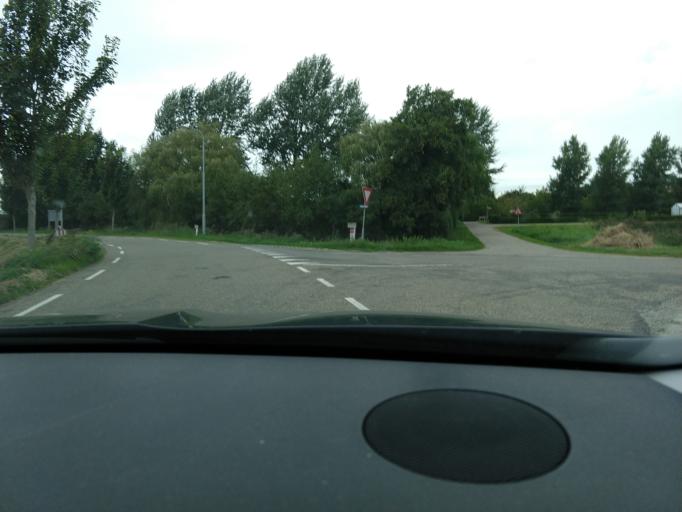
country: NL
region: Zeeland
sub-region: Gemeente Goes
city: Goes
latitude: 51.4140
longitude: 3.8824
